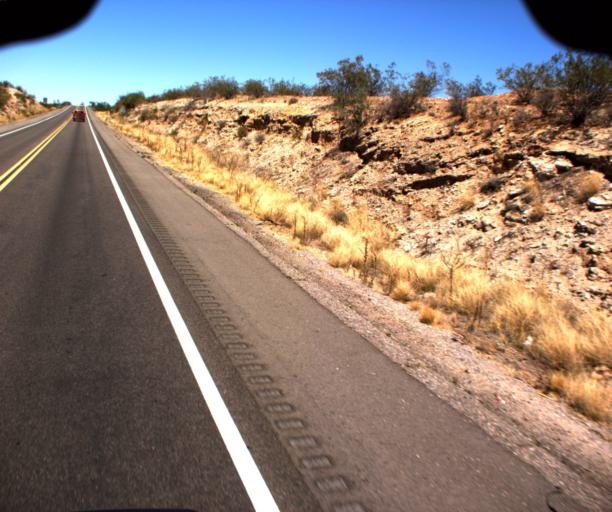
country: US
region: Arizona
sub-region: Maricopa County
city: Wickenburg
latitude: 34.0281
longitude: -112.8130
